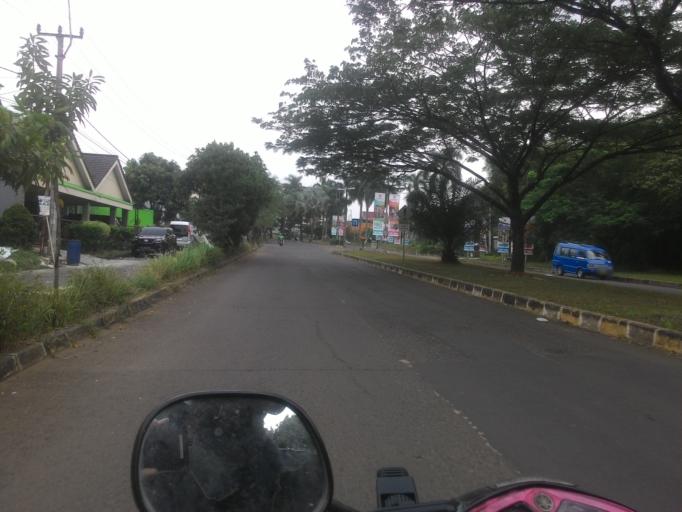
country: ID
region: West Java
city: Depok
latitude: -6.4427
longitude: 106.8288
